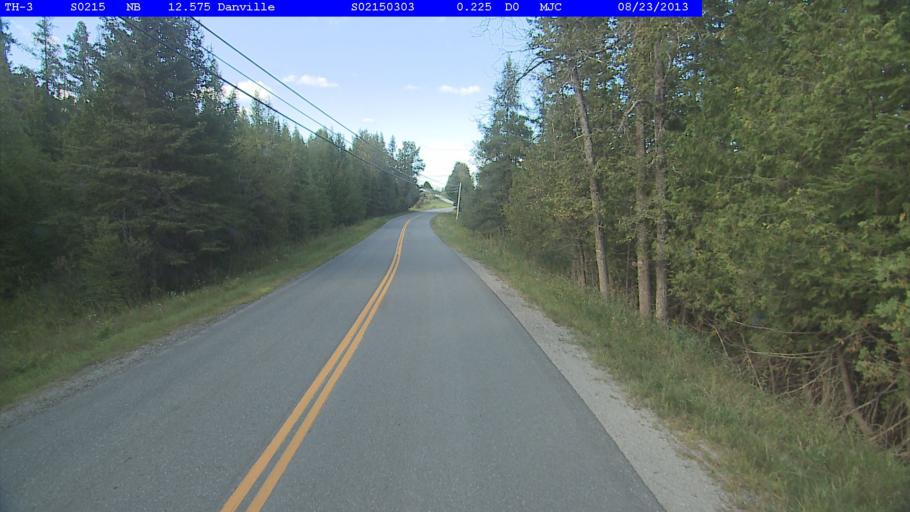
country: US
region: Vermont
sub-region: Caledonia County
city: Saint Johnsbury
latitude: 44.3691
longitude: -72.1476
